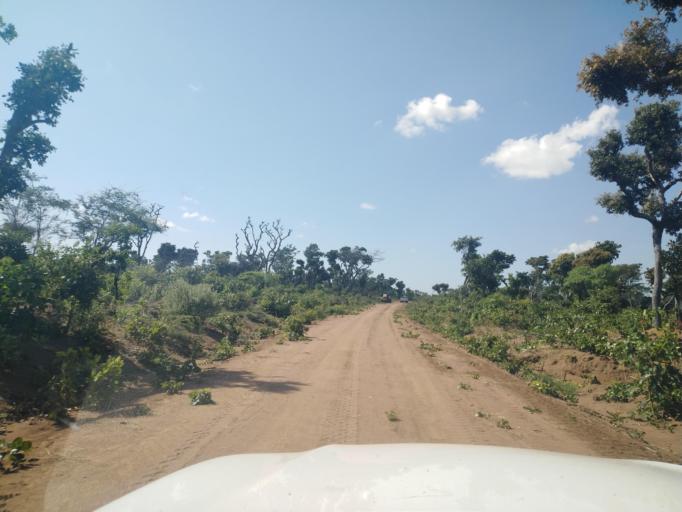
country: ZM
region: Northern
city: Chinsali
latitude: -11.0085
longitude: 31.7742
